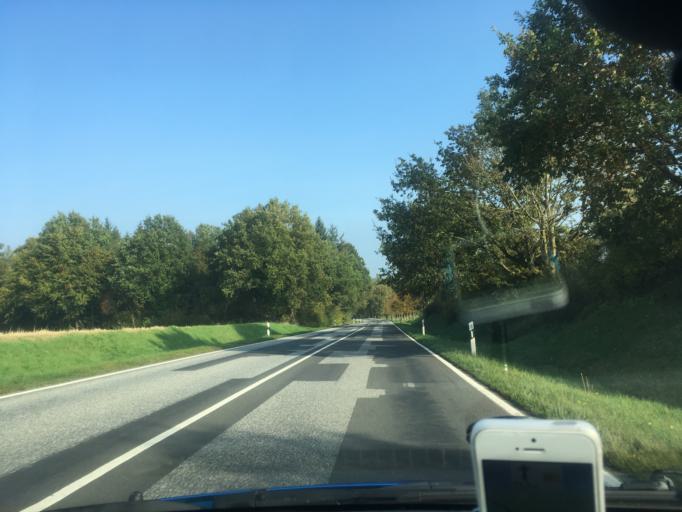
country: DE
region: Mecklenburg-Vorpommern
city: Hagenow
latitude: 53.4503
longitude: 11.2183
